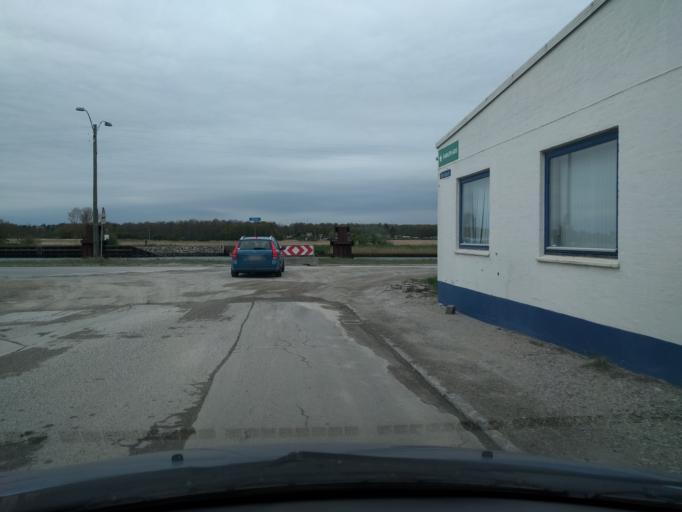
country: DK
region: South Denmark
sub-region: Odense Kommune
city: Odense
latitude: 55.4239
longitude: 10.3839
